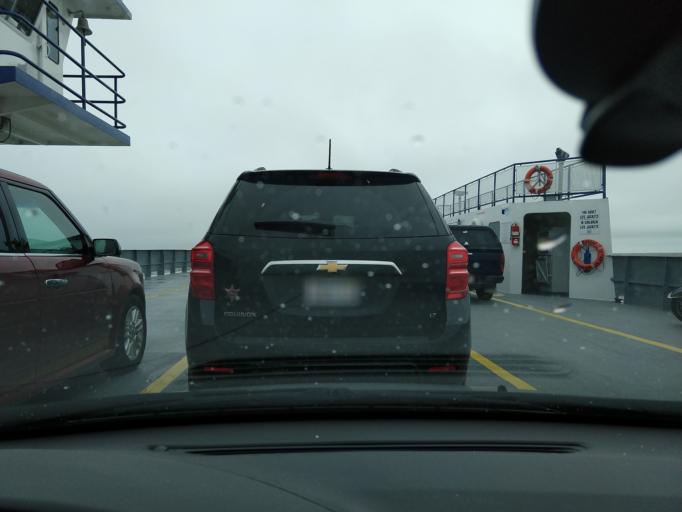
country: US
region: Alabama
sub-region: Mobile County
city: Dauphin Island
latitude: 30.2481
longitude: -88.0483
